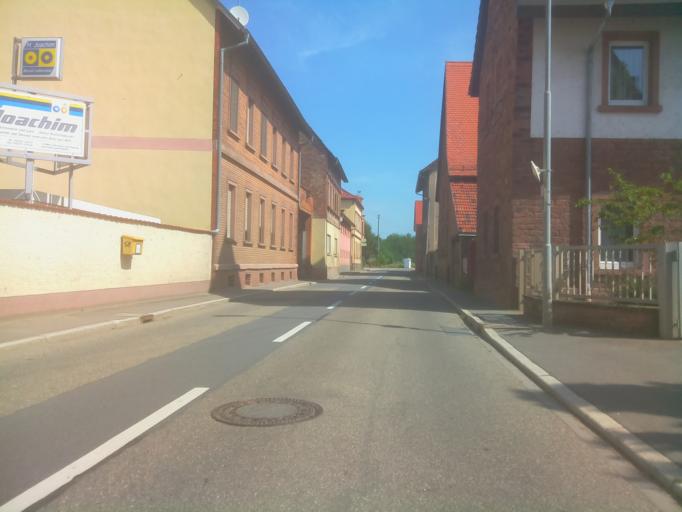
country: DE
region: Baden-Wuerttemberg
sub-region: Karlsruhe Region
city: Heddesheim
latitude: 49.5288
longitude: 8.6183
